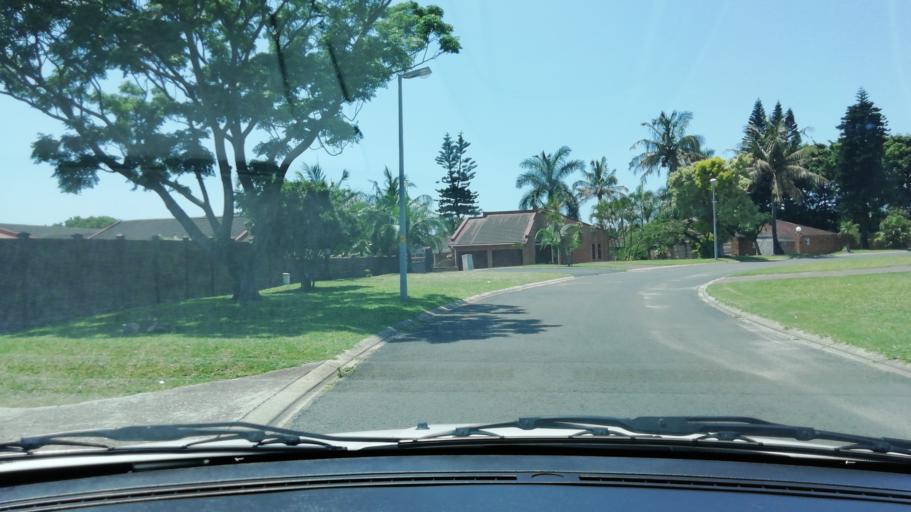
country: ZA
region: KwaZulu-Natal
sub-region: uThungulu District Municipality
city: Richards Bay
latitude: -28.7342
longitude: 32.0458
